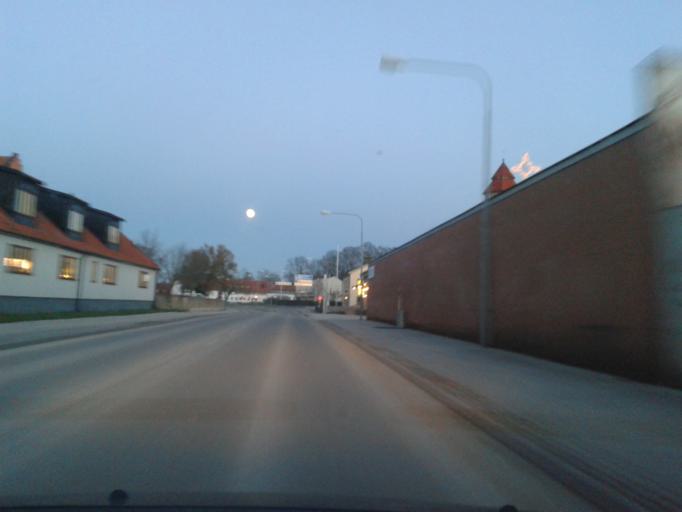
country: SE
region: Gotland
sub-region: Gotland
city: Visby
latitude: 57.6324
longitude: 18.2917
